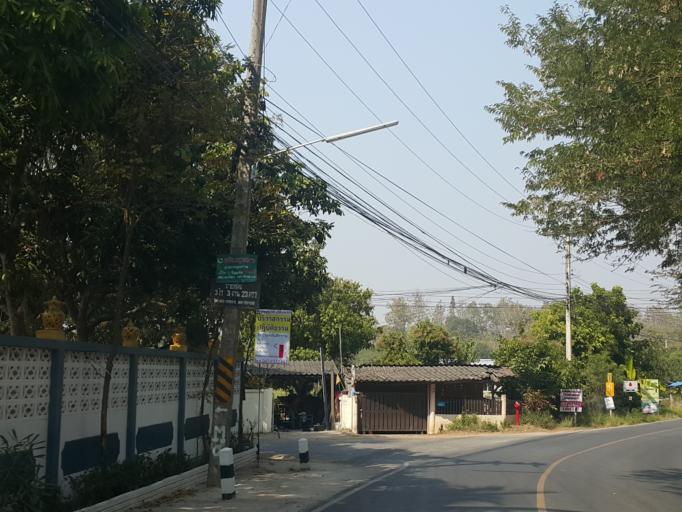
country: TH
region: Chiang Mai
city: Mae Taeng
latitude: 18.9611
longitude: 98.9217
